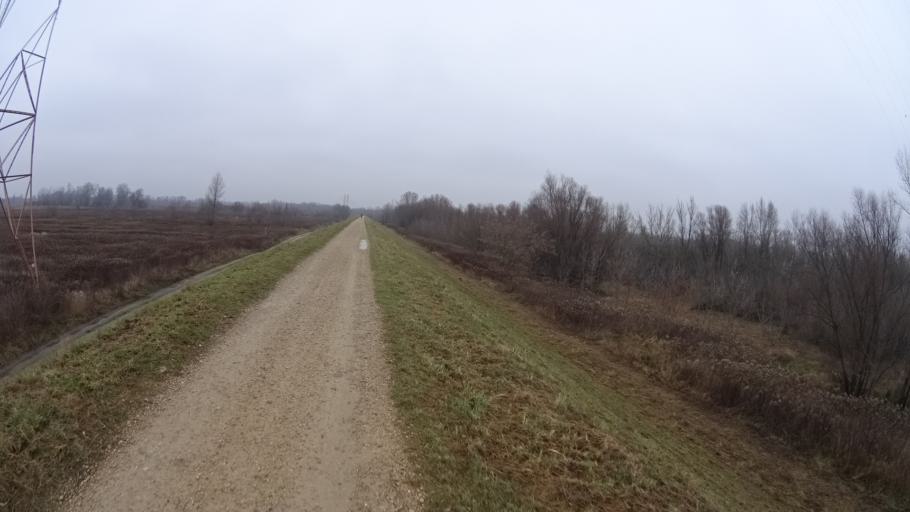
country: PL
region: Masovian Voivodeship
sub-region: Warszawa
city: Wilanow
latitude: 52.1983
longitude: 21.0995
